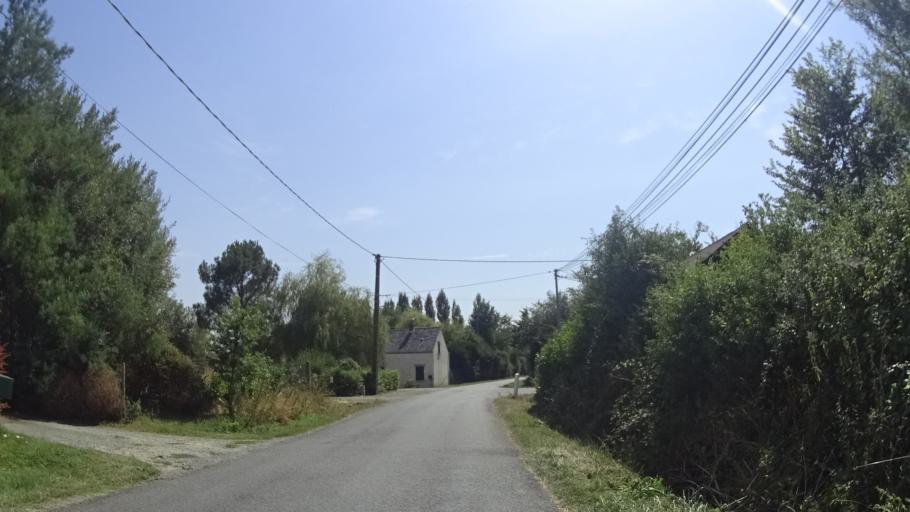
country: FR
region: Pays de la Loire
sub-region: Departement de la Loire-Atlantique
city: Prinquiau
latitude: 47.3468
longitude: -2.0024
